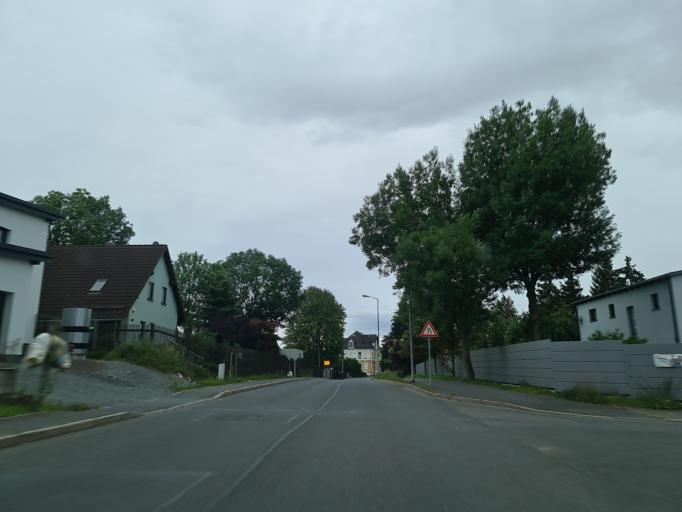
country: DE
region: Saxony
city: Plauen
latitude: 50.4996
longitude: 12.0995
